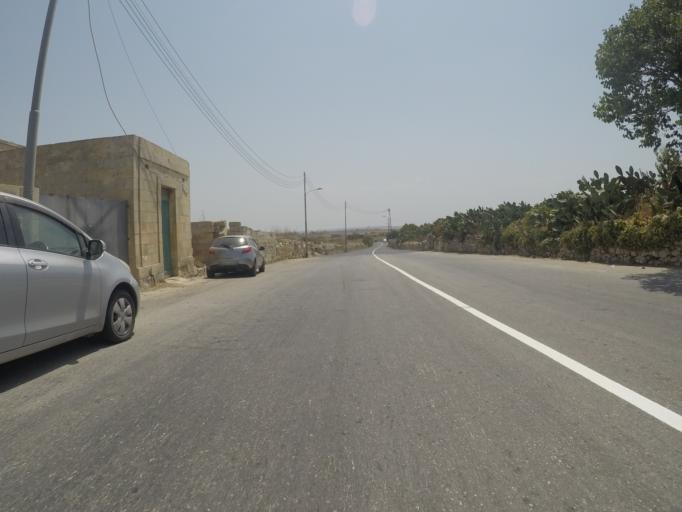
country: MT
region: L-Imdina
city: Imdina
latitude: 35.8813
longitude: 14.4077
